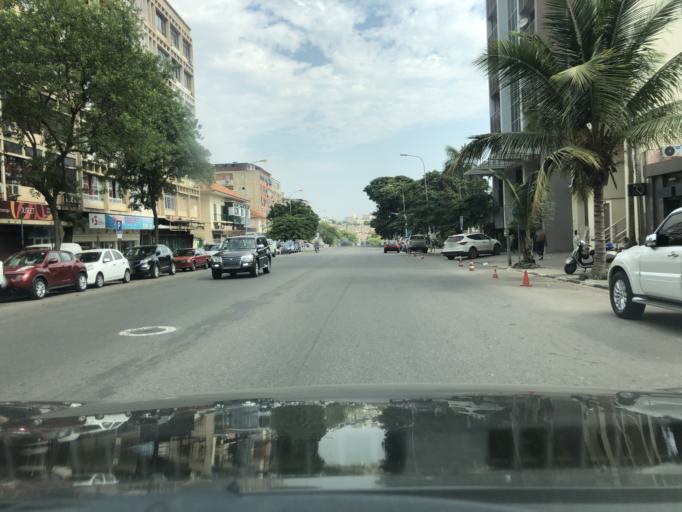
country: AO
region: Luanda
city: Luanda
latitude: -8.8248
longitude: 13.2282
